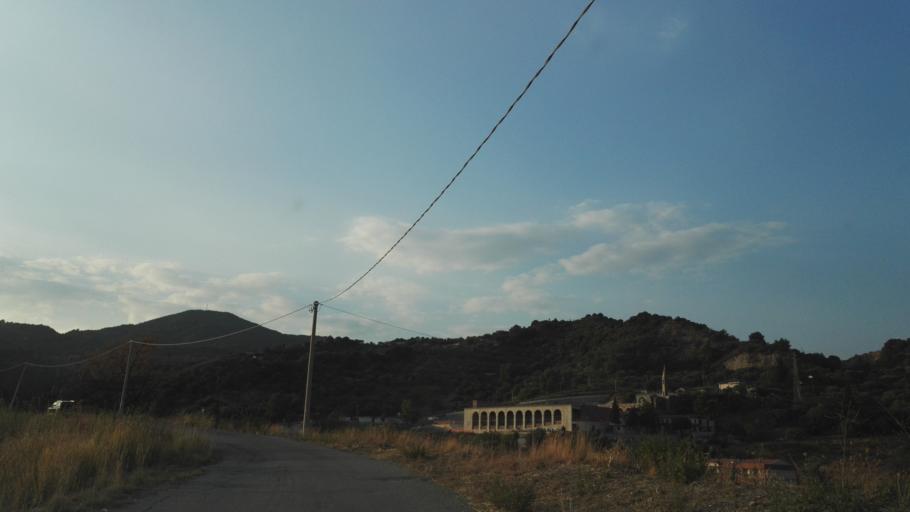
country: IT
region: Calabria
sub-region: Provincia di Reggio Calabria
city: Placanica
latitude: 38.4053
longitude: 16.4283
